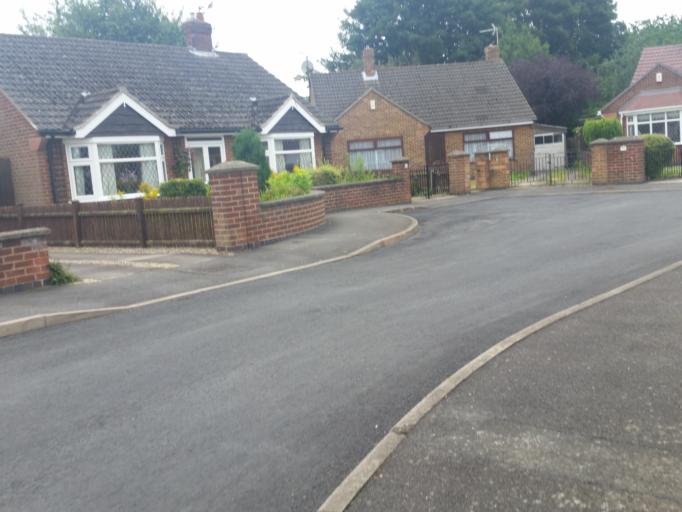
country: GB
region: England
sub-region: Derbyshire
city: Borrowash
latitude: 52.8921
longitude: -1.4200
